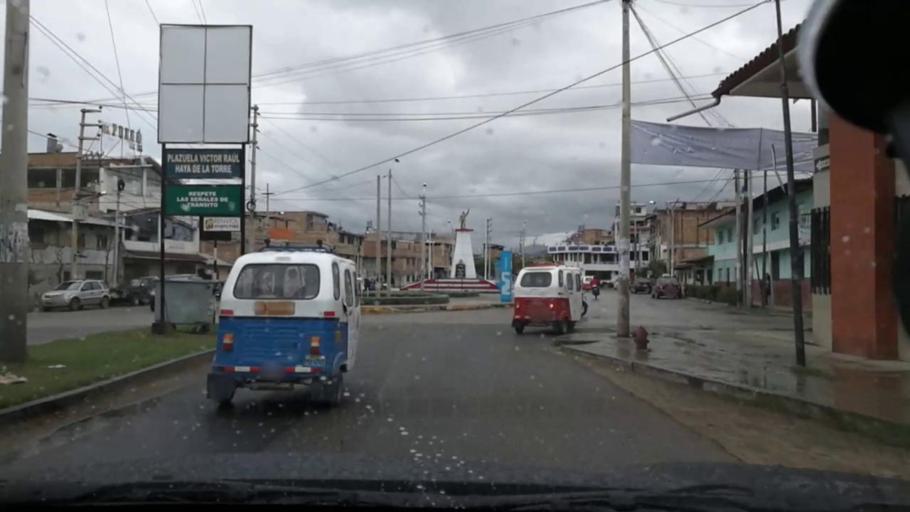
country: PE
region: Cajamarca
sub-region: Provincia de Cajamarca
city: Cajamarca
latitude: -7.1606
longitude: -78.5075
